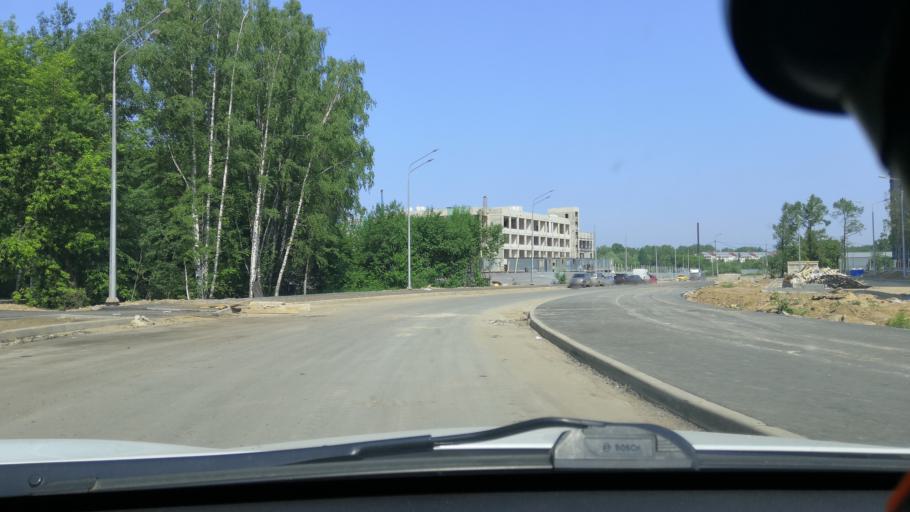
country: RU
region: Moscow
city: Severnyy
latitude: 55.9397
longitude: 37.5248
